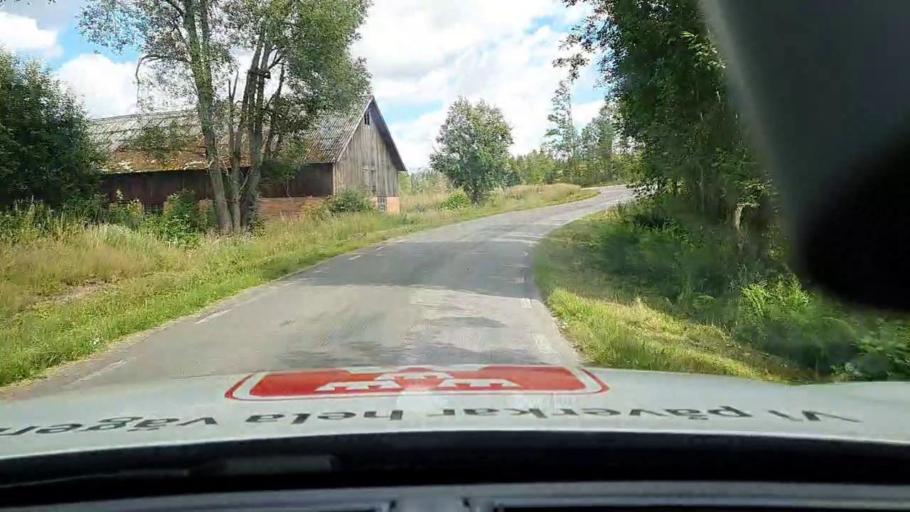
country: SE
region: Vaestra Goetaland
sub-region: Karlsborgs Kommun
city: Molltorp
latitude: 58.6045
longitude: 14.2850
